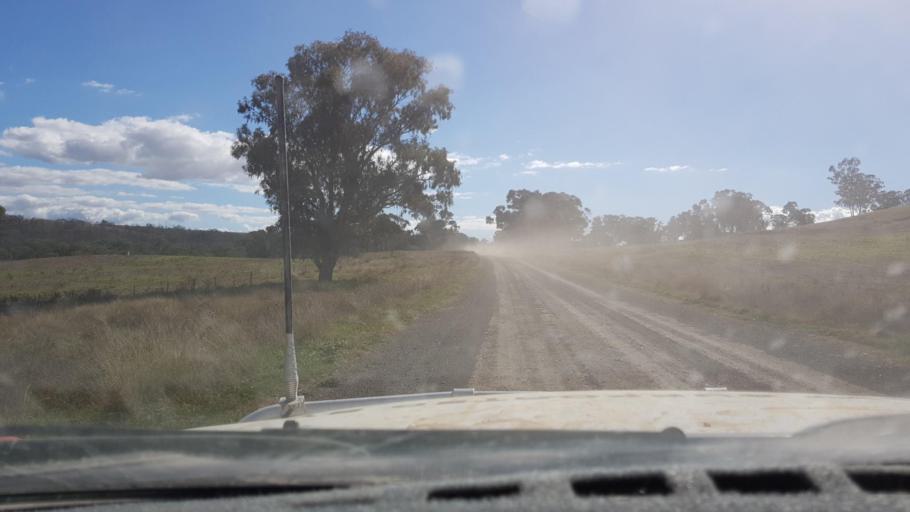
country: AU
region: New South Wales
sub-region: Narrabri
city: Blair Athol
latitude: -30.4314
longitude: 150.4573
